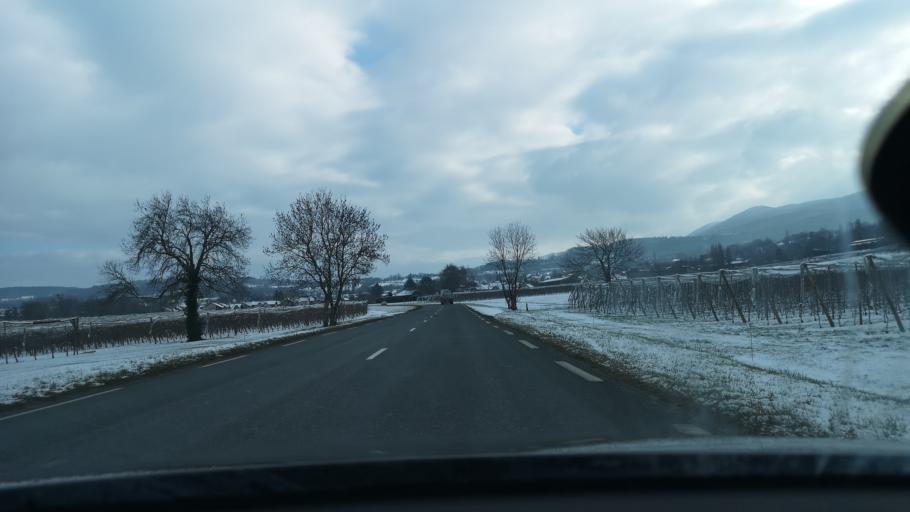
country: FR
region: Rhone-Alpes
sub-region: Departement de l'Ain
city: Collonges
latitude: 46.1088
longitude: 5.9236
